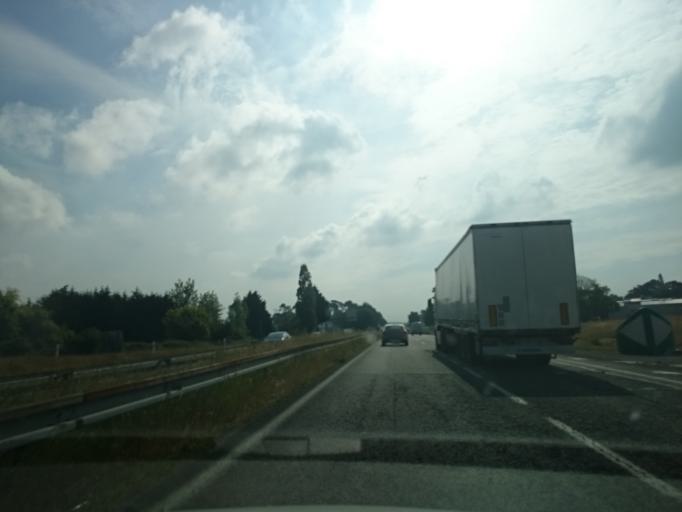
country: FR
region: Brittany
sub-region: Departement du Morbihan
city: Ploeren
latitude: 47.6607
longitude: -2.8596
